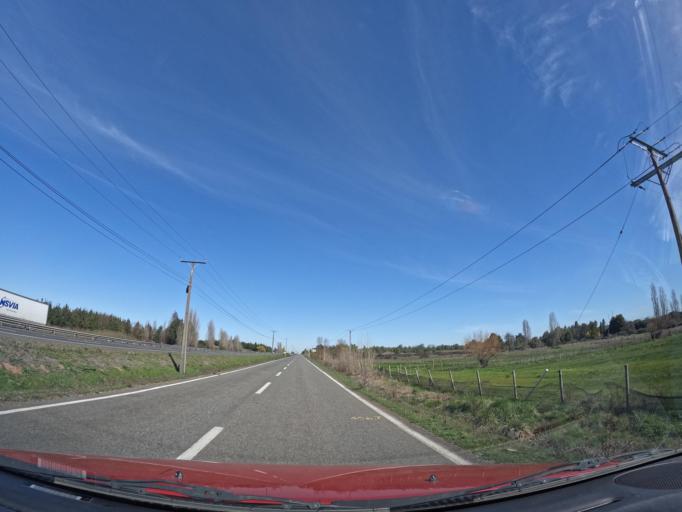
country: CL
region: Biobio
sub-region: Provincia de Biobio
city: Cabrero
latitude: -37.0158
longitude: -72.3656
